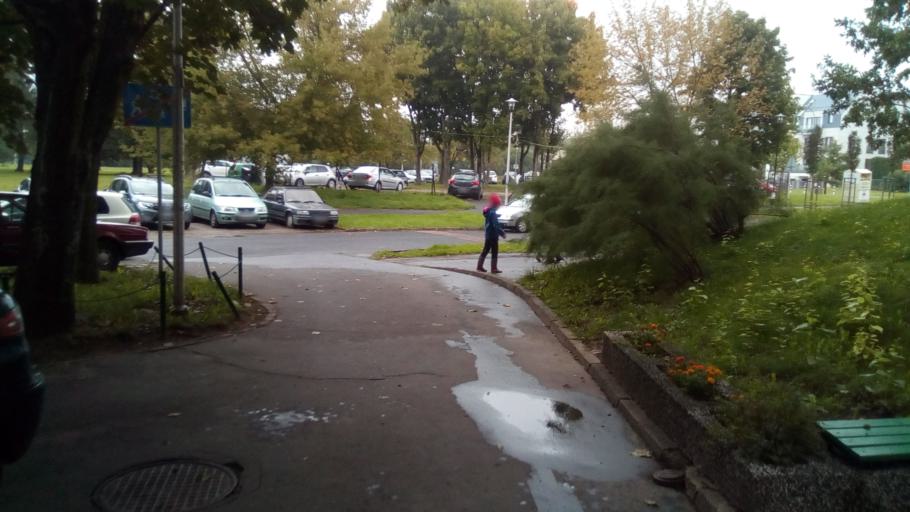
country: PL
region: Masovian Voivodeship
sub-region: Warszawa
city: Ursynow
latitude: 52.1588
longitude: 21.0537
